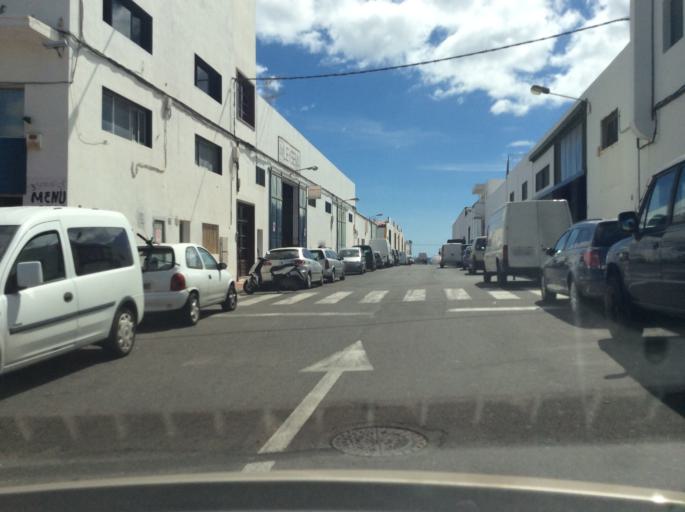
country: ES
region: Canary Islands
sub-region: Provincia de Las Palmas
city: Arrecife
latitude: 28.9742
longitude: -13.5345
